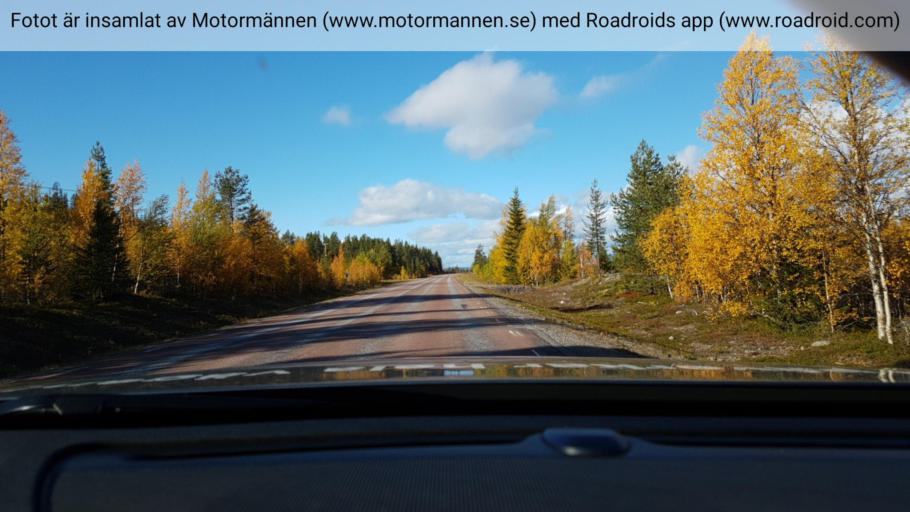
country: SE
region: Norrbotten
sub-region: Arjeplogs Kommun
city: Arjeplog
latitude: 66.0570
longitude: 17.9801
